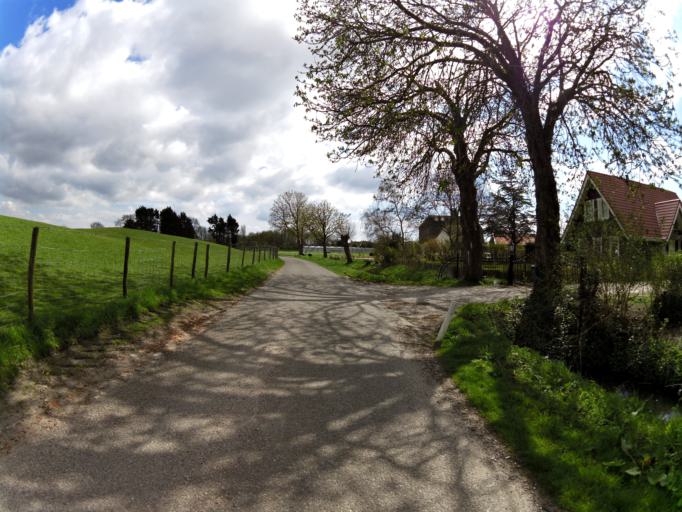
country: NL
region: South Holland
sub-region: Gemeente Hellevoetsluis
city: Nieuw-Helvoet
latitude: 51.8945
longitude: 4.0793
